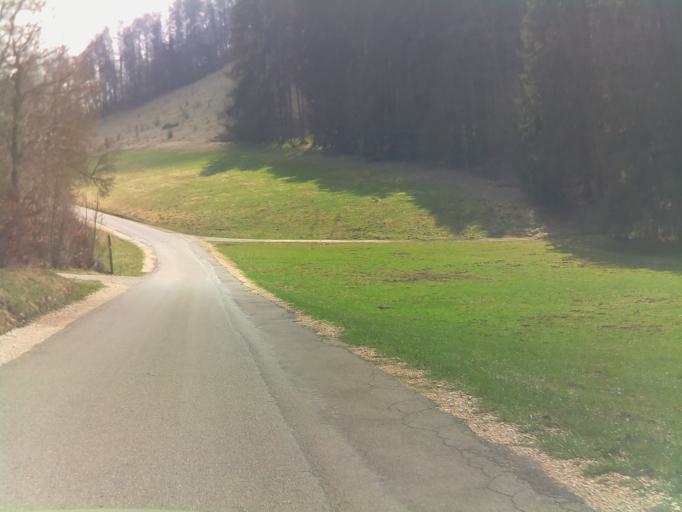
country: DE
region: Baden-Wuerttemberg
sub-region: Tuebingen Region
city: Gomadingen
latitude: 48.4337
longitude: 9.4291
